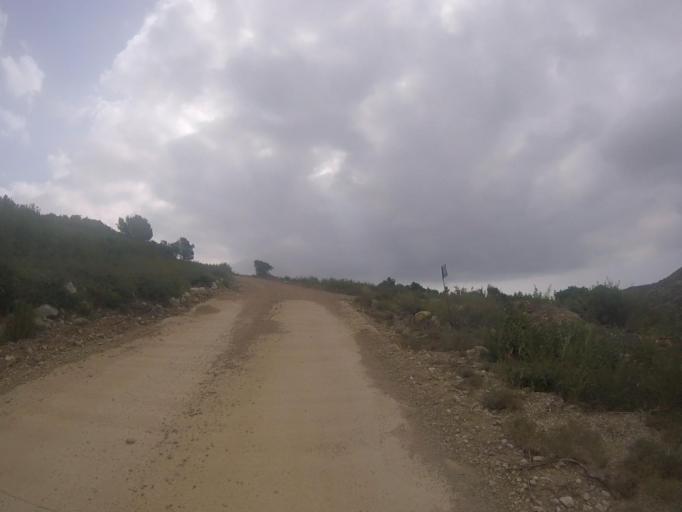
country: ES
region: Valencia
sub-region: Provincia de Castello
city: Santa Magdalena de Pulpis
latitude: 40.3457
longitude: 0.3232
